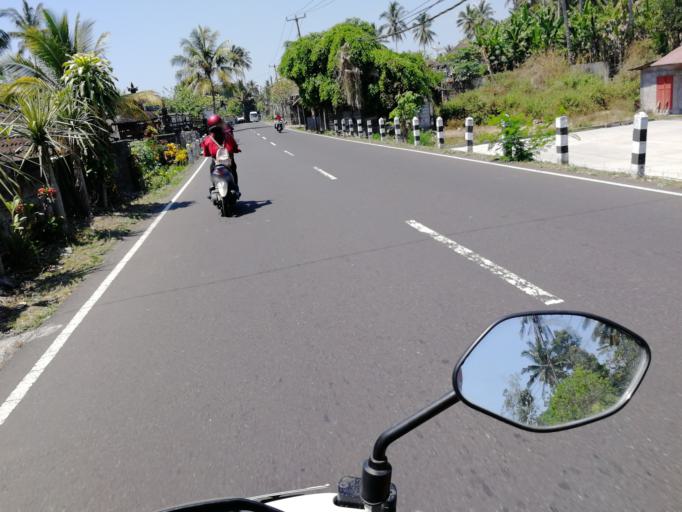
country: ID
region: Bali
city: Abang
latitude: -8.3978
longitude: 115.5961
